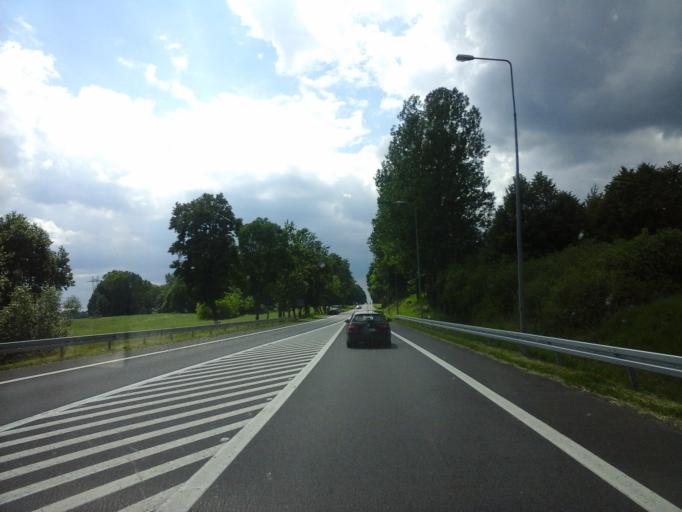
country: PL
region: West Pomeranian Voivodeship
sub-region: Powiat bialogardzki
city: Karlino
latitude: 54.0253
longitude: 15.8594
